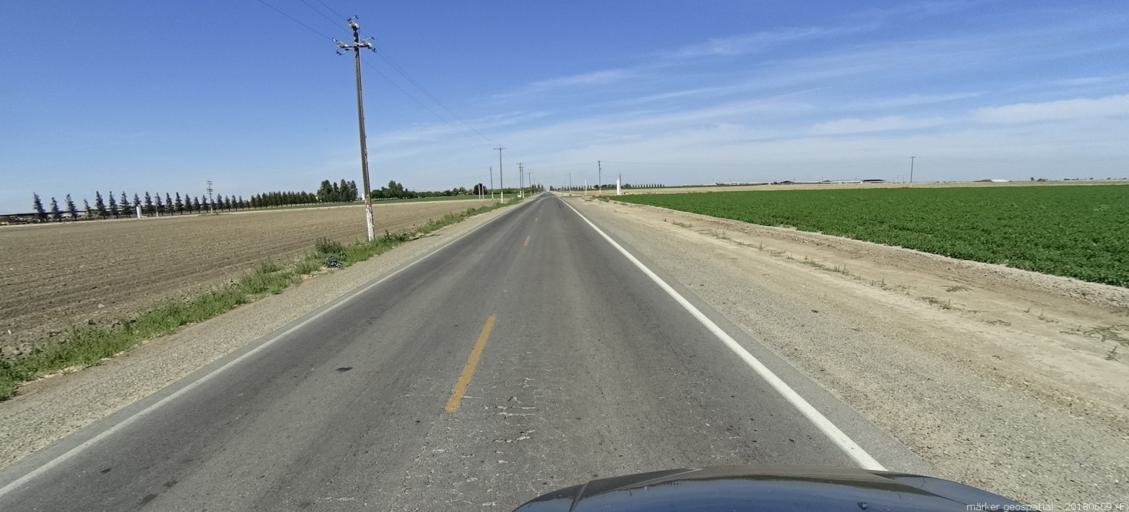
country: US
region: California
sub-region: Madera County
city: Fairmead
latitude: 36.9528
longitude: -120.2717
